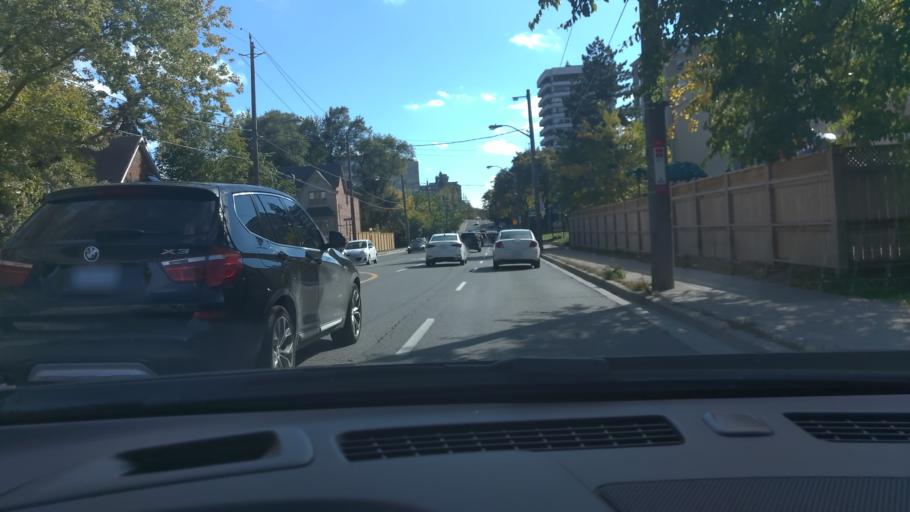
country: CA
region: Ontario
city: Toronto
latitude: 43.7103
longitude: -79.4277
